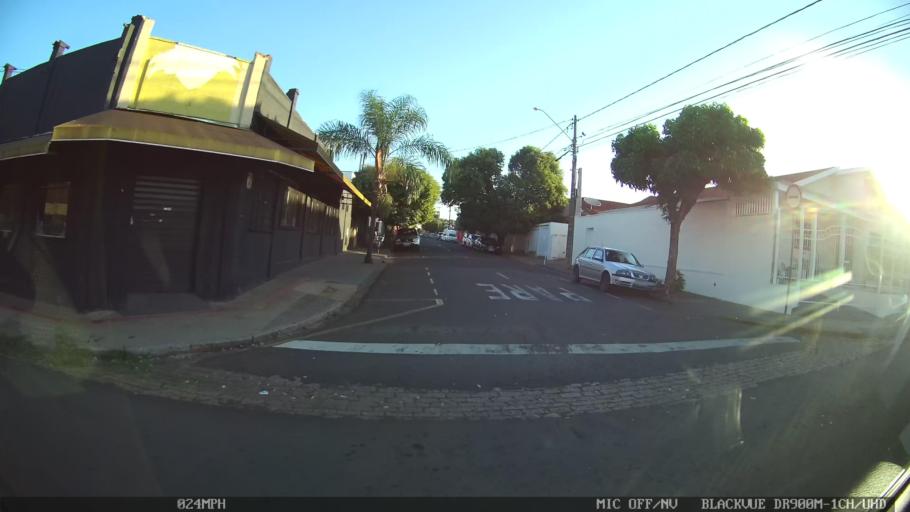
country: BR
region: Sao Paulo
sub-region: Sao Jose Do Rio Preto
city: Sao Jose do Rio Preto
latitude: -20.8014
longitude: -49.3859
